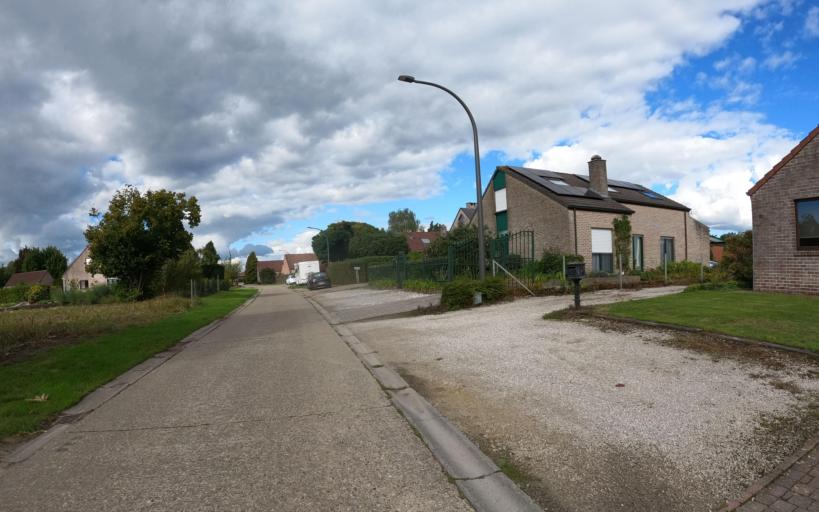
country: BE
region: Flanders
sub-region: Provincie Antwerpen
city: Heist-op-den-Berg
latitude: 51.1071
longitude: 4.7229
